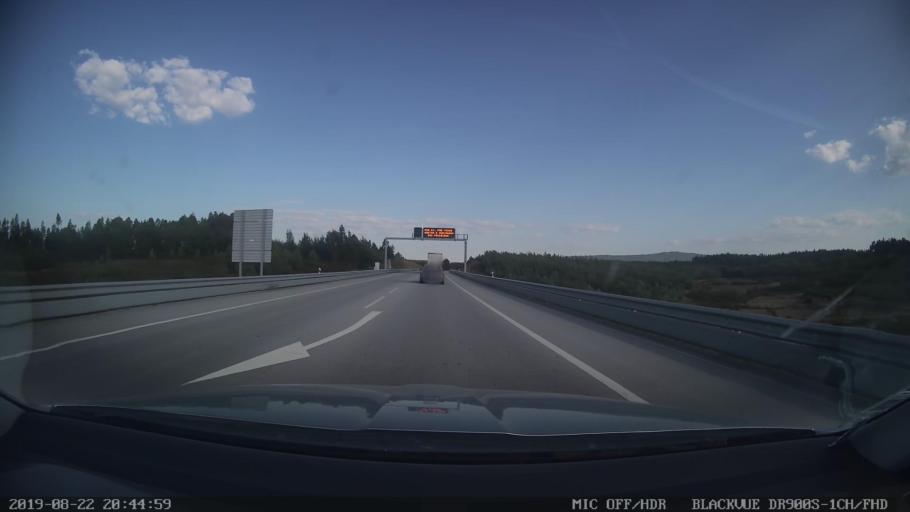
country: PT
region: Castelo Branco
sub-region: Proenca-A-Nova
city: Proenca-a-Nova
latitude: 39.7121
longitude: -7.8605
